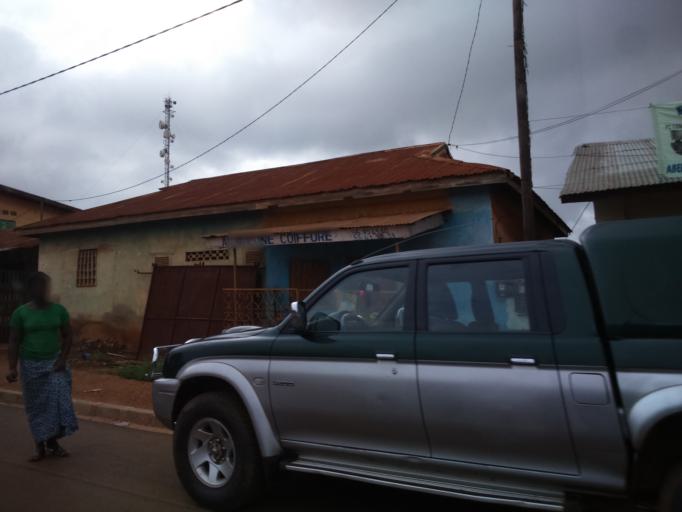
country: CI
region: Moyen-Comoe
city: Abengourou
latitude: 6.7287
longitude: -3.4866
